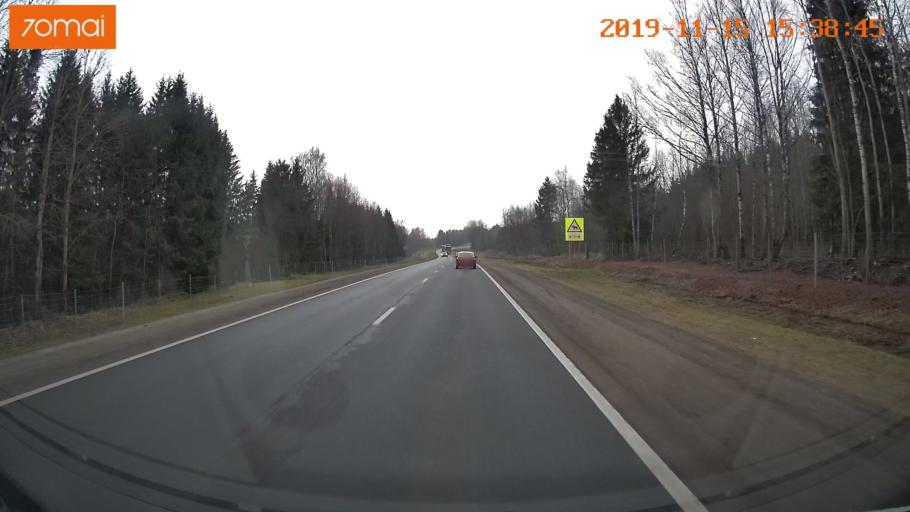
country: RU
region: Jaroslavl
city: Danilov
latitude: 58.0269
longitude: 40.0766
